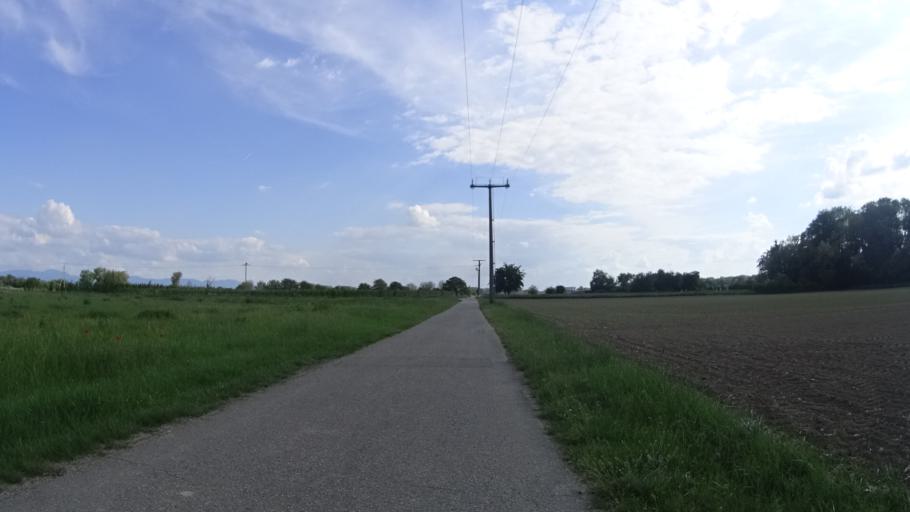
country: DE
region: Baden-Wuerttemberg
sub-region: Freiburg Region
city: Breisach am Rhein
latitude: 48.0635
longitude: 7.5894
